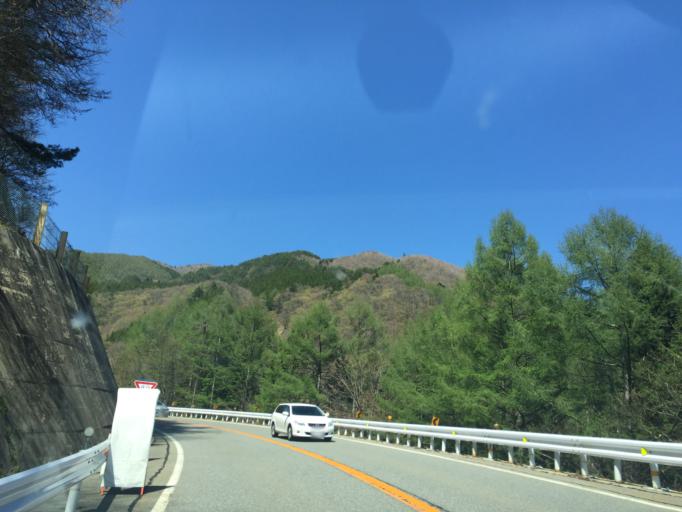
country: JP
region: Gifu
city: Nakatsugawa
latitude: 35.3428
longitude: 137.6491
